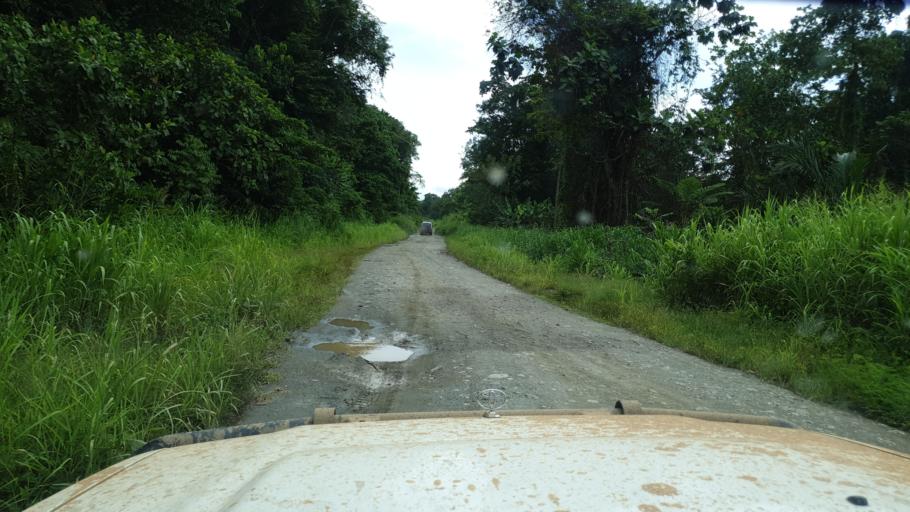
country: PG
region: Northern Province
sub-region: Sohe
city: Kokoda
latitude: -8.9162
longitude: 147.8530
